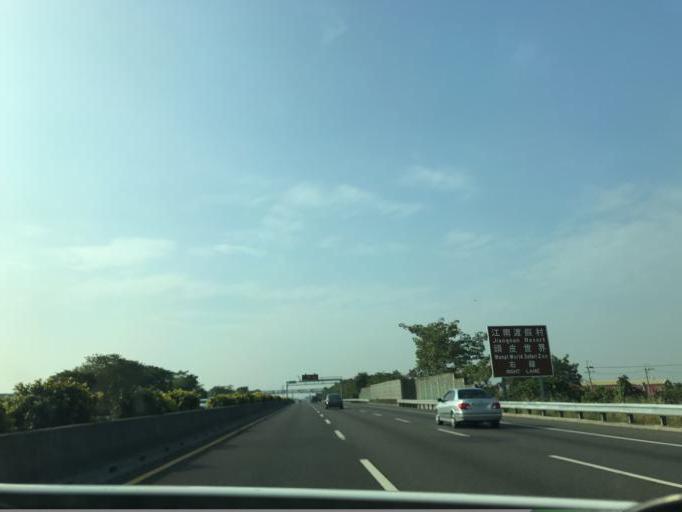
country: TW
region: Taiwan
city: Xinying
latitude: 23.3245
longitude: 120.3005
